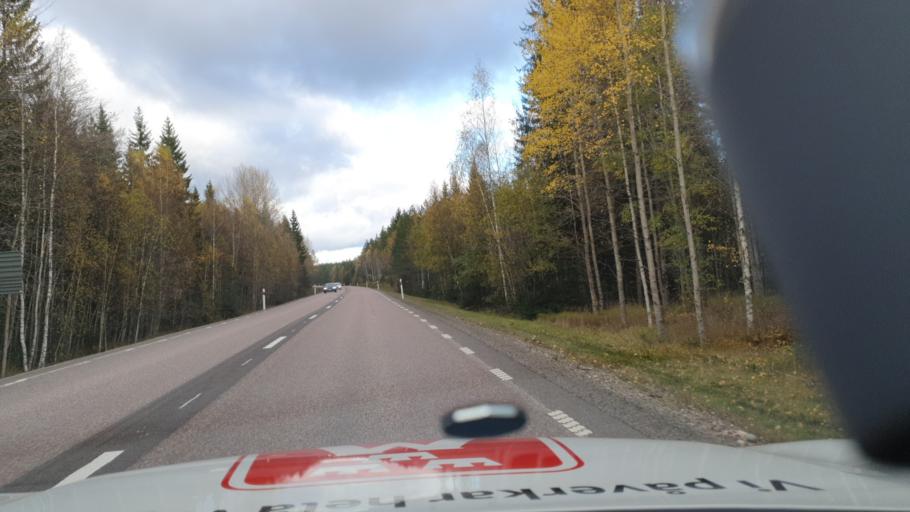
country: SE
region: Gaevleborg
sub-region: Gavle Kommun
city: Hedesunda
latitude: 60.3451
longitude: 16.9515
